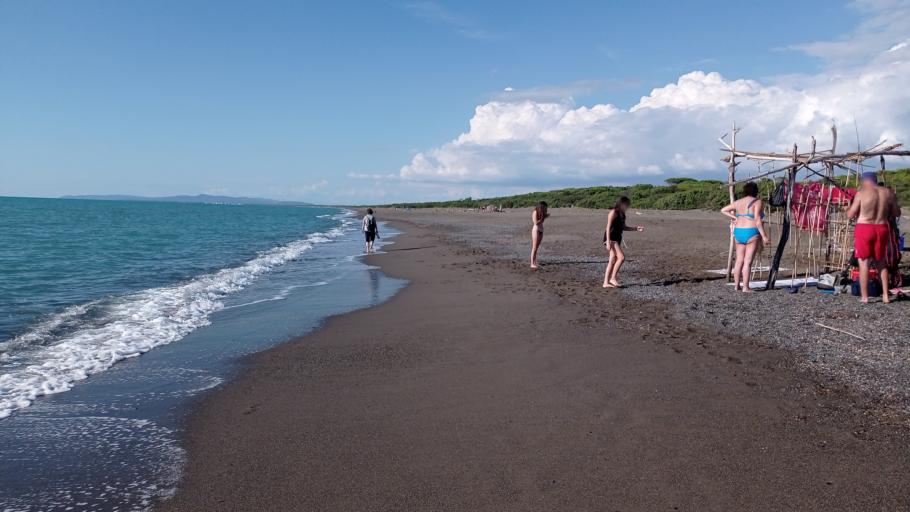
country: IT
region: Tuscany
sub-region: Provincia di Livorno
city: Donoratico
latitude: 43.1958
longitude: 10.5351
